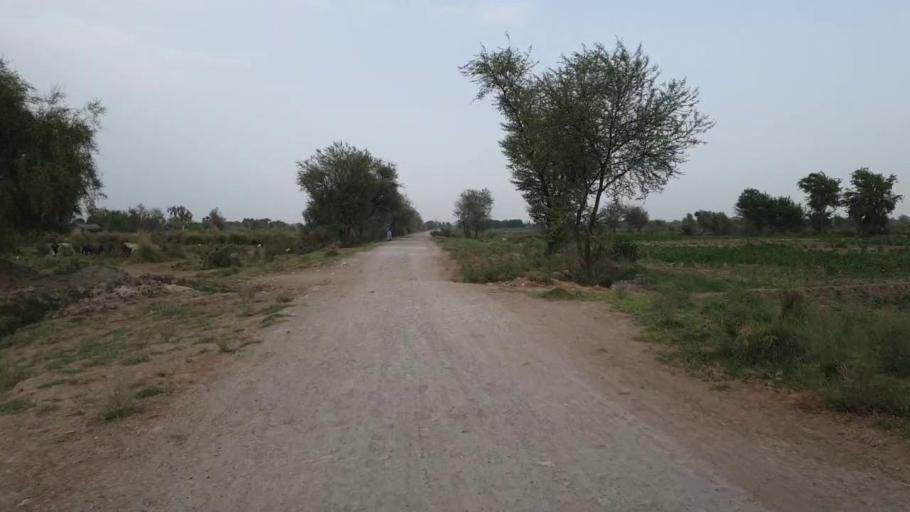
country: PK
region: Sindh
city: Bandhi
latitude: 26.5191
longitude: 68.1817
